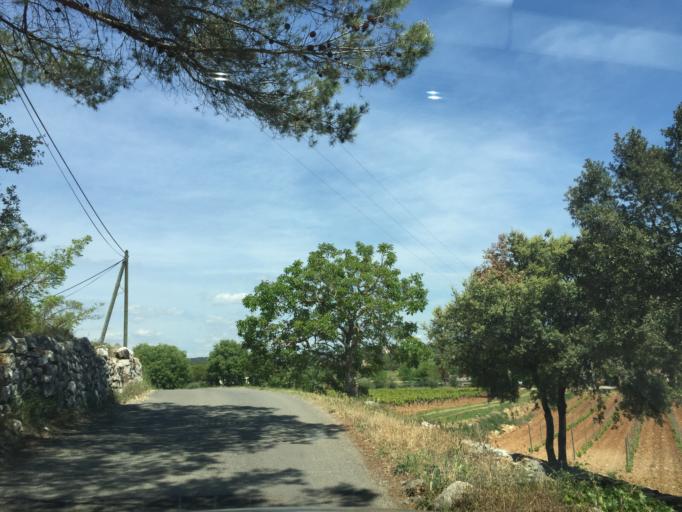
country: FR
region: Provence-Alpes-Cote d'Azur
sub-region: Departement du Var
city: Lorgues
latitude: 43.4774
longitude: 6.3679
